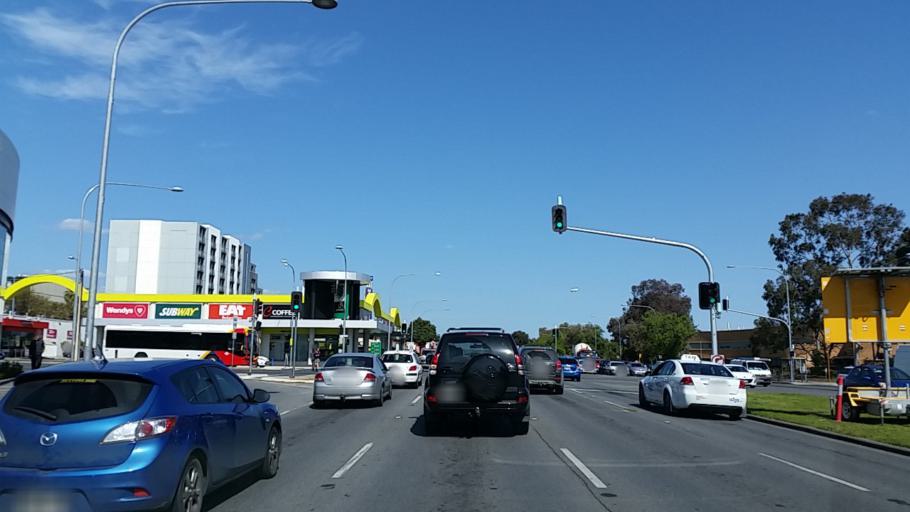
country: AU
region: South Australia
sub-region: Adelaide
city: Adelaide
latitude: -34.9244
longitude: 138.5876
